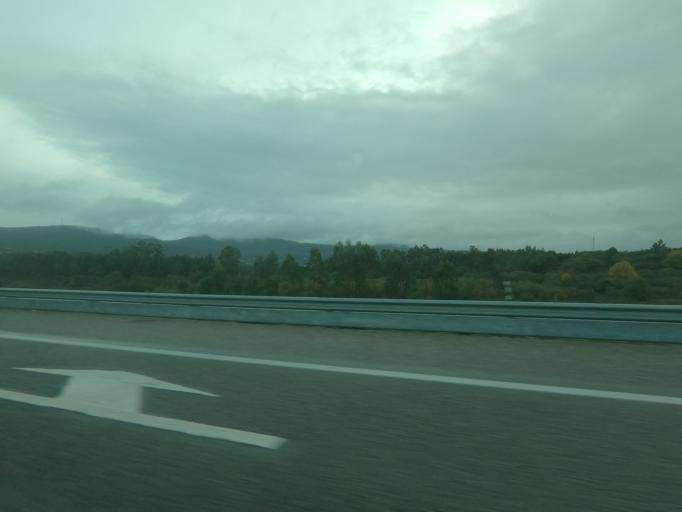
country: PT
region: Viana do Castelo
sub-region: Valenca
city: Valenza
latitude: 41.9833
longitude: -8.6490
